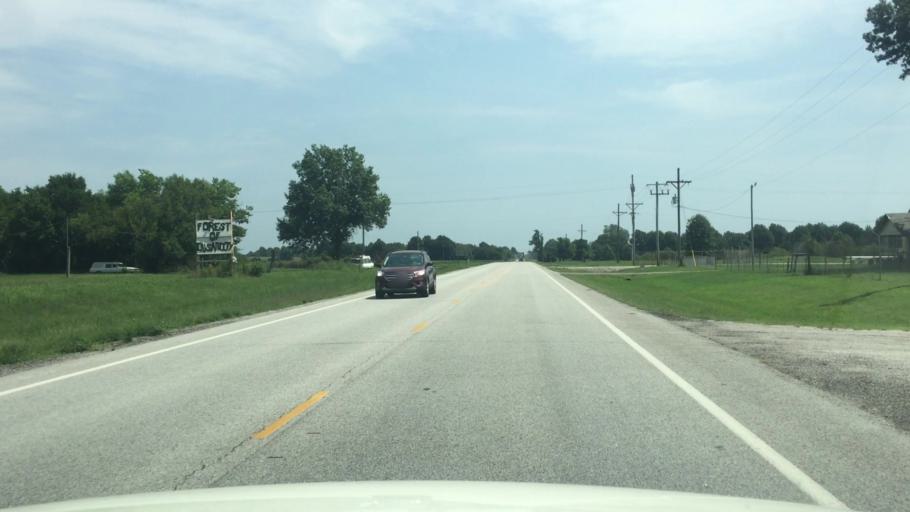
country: US
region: Kansas
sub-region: Cherokee County
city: Columbus
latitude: 37.1781
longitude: -94.8150
